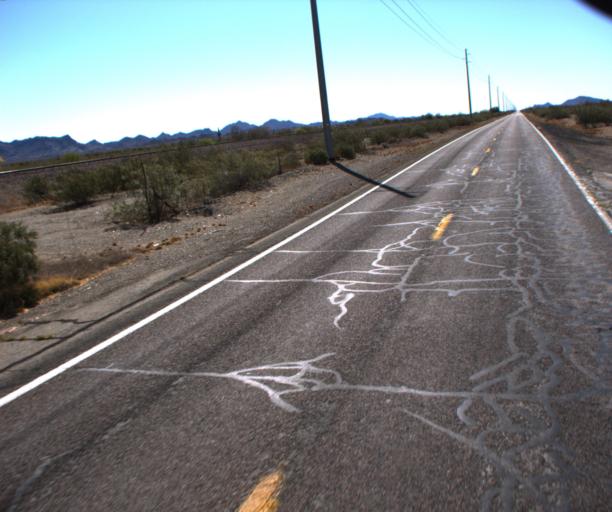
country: US
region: Arizona
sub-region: La Paz County
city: Salome
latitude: 33.7923
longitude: -113.8228
